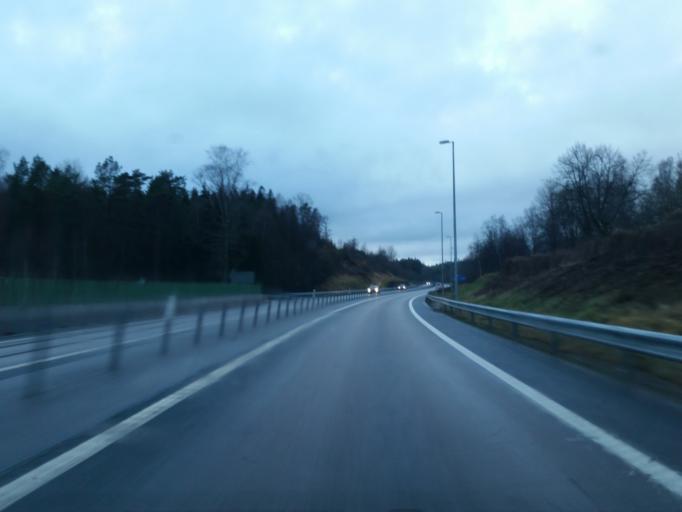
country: SE
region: Vaestra Goetaland
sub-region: Boras Kommun
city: Boras
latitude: 57.6805
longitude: 12.9587
